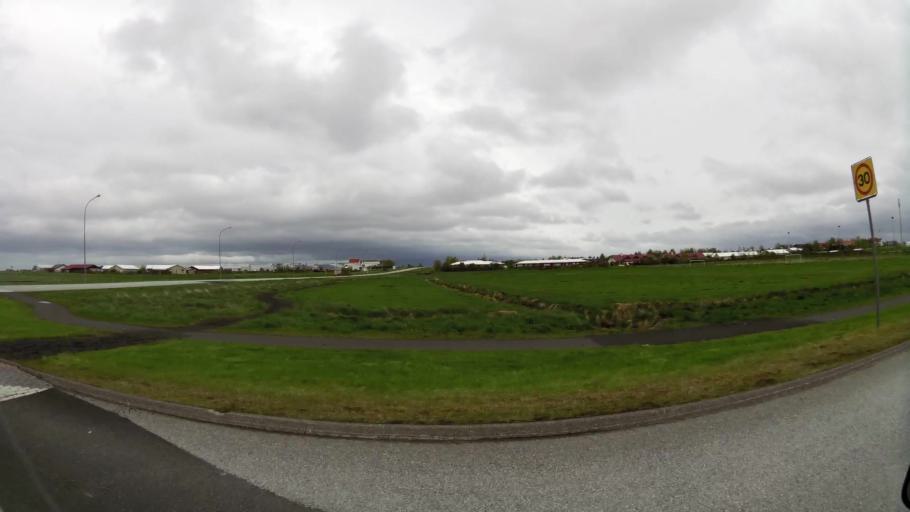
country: IS
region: Capital Region
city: Alftanes
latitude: 64.1062
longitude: -22.0253
